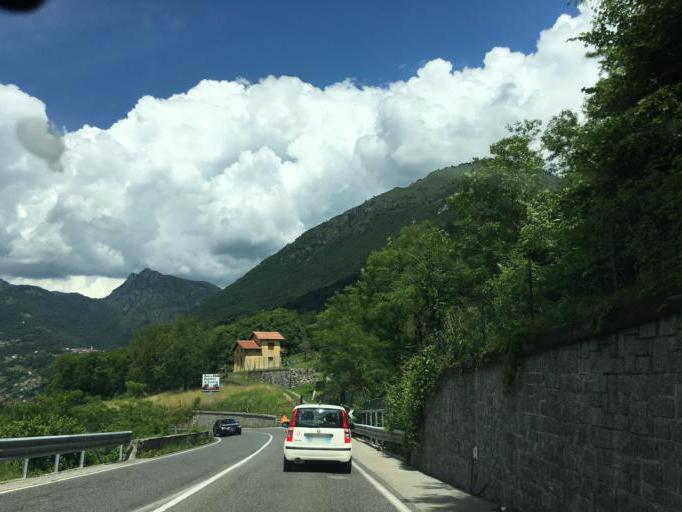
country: IT
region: Lombardy
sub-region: Provincia di Como
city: Bene Lario
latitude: 46.0356
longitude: 9.1863
